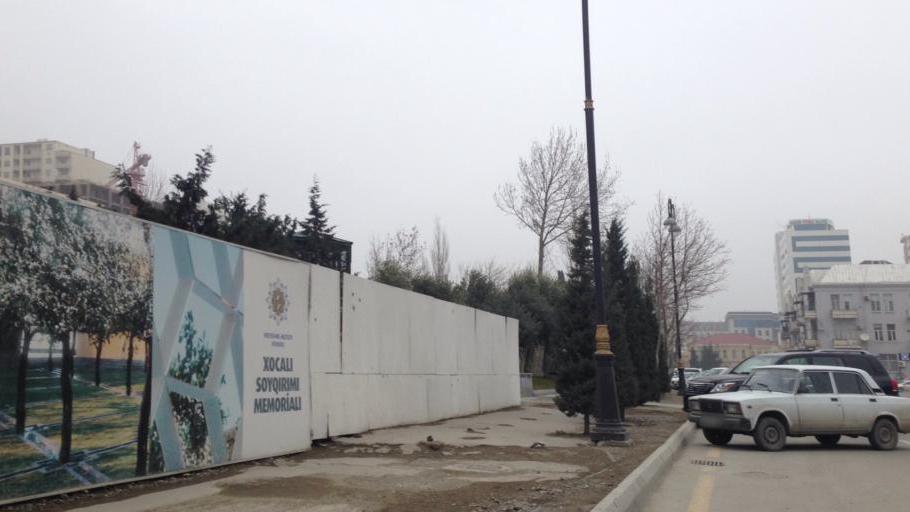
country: AZ
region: Baki
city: Baku
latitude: 40.3832
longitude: 49.8739
